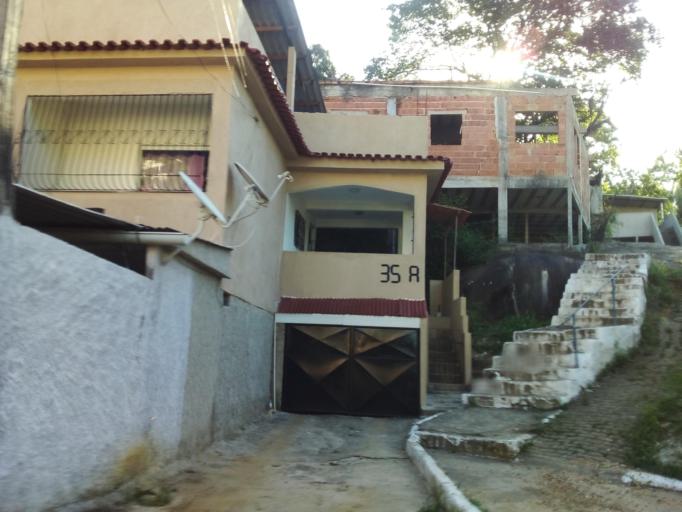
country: BR
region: Espirito Santo
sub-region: Vitoria
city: Vitoria
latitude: -20.3291
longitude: -40.3454
